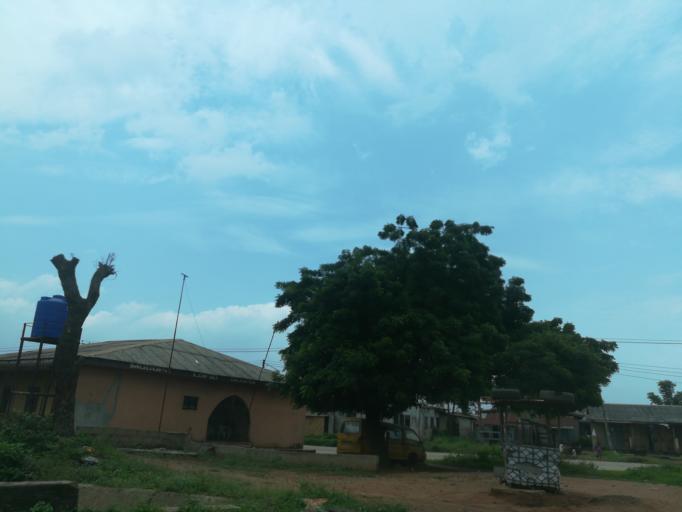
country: NG
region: Lagos
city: Ikorodu
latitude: 6.5641
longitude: 3.5976
